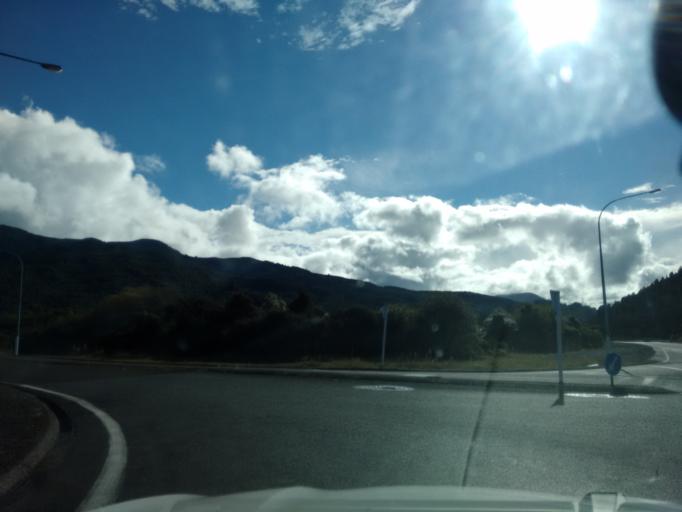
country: NZ
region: Waikato
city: Turangi
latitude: -38.9819
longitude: 175.7797
